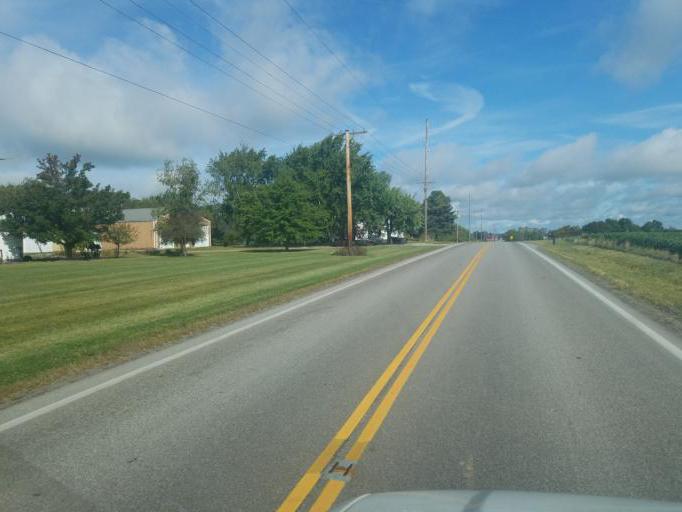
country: US
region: Ohio
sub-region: Wayne County
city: West Salem
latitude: 41.0020
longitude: -82.1143
